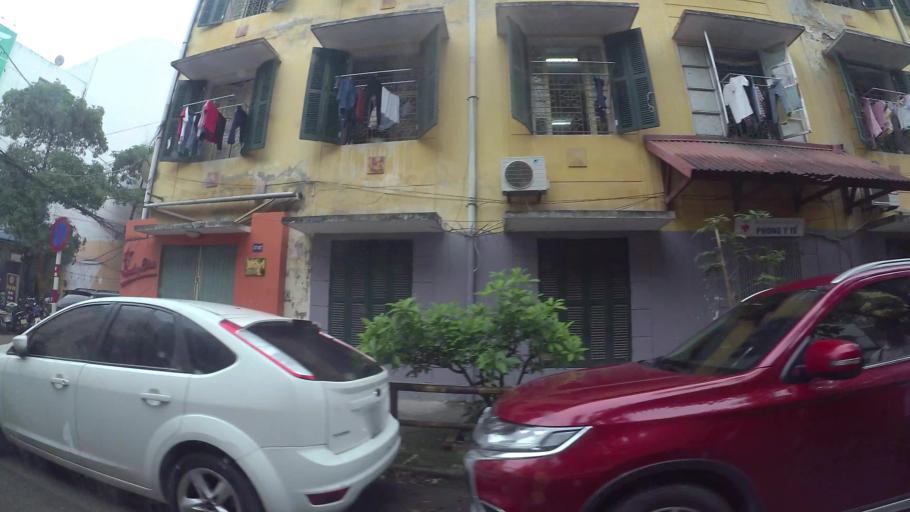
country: VN
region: Ha Noi
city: Dong Da
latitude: 21.0096
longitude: 105.8272
